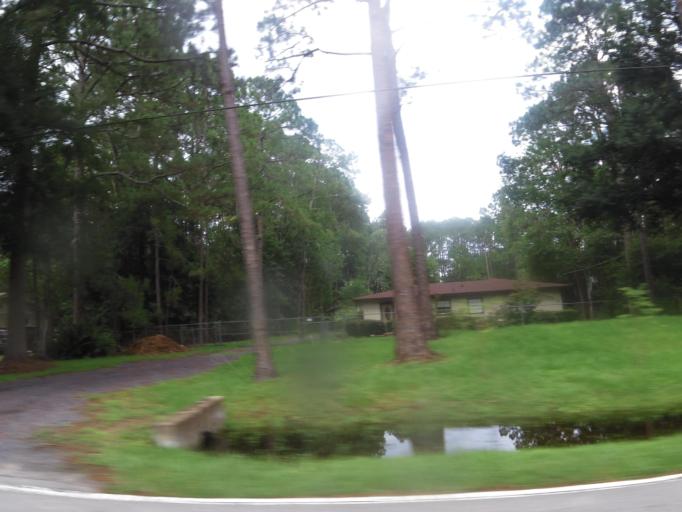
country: US
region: Florida
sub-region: Duval County
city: Jacksonville
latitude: 30.2950
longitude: -81.5294
